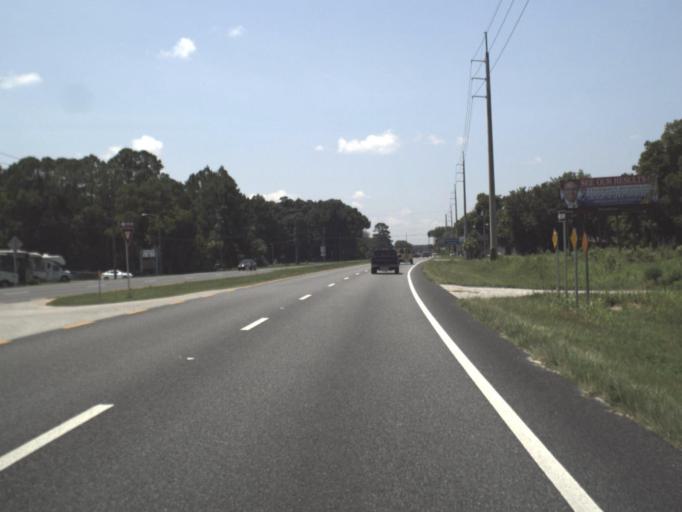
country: US
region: Florida
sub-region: Citrus County
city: Homosassa Springs
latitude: 28.8140
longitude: -82.5767
